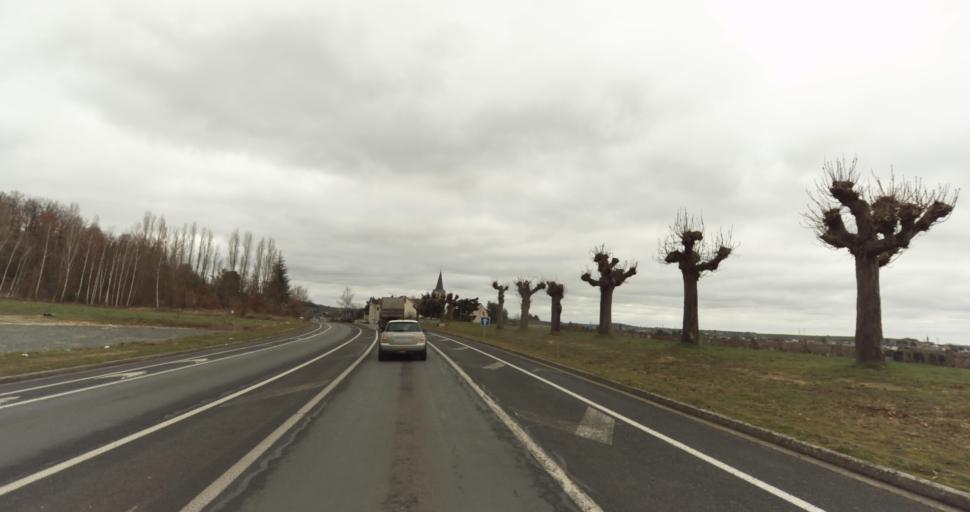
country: FR
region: Pays de la Loire
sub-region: Departement de Maine-et-Loire
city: Varrains
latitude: 47.2282
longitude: -0.0696
